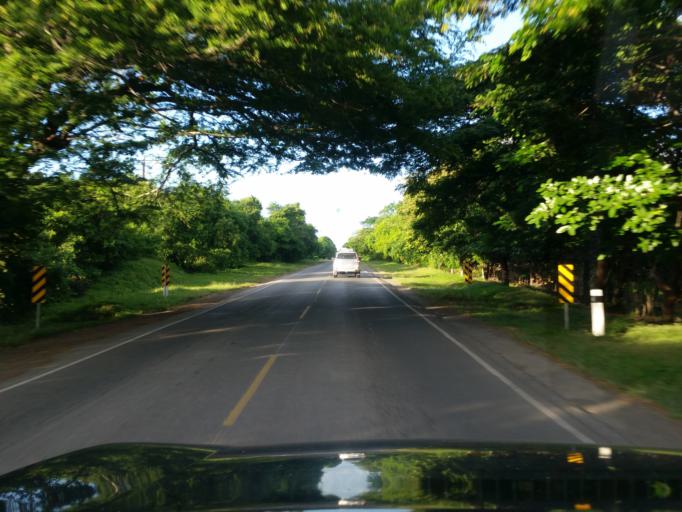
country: NI
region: Granada
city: Nandaime
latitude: 11.7960
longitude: -86.0476
